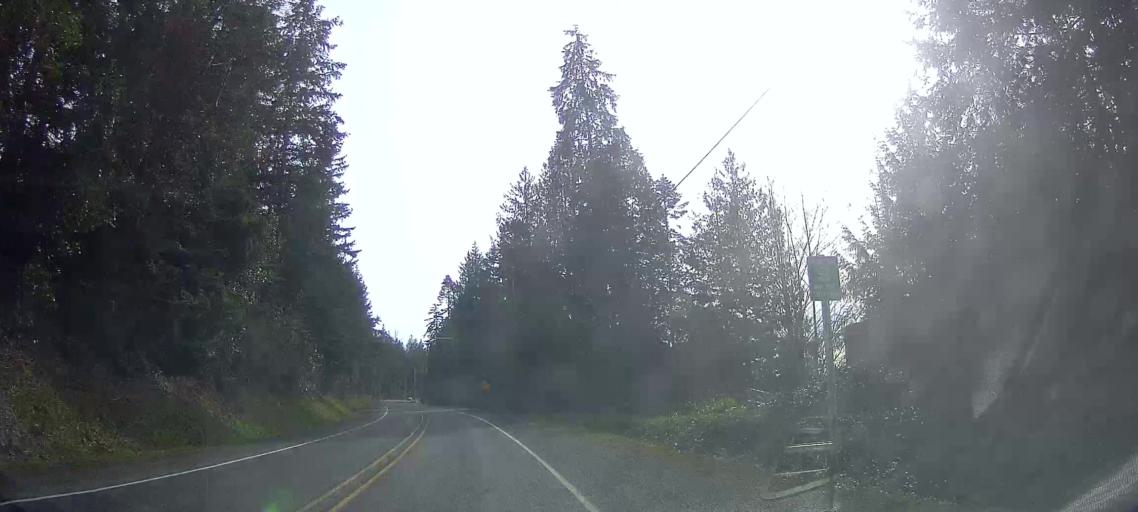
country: US
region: Washington
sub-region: Island County
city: Camano
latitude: 48.1368
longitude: -122.4664
